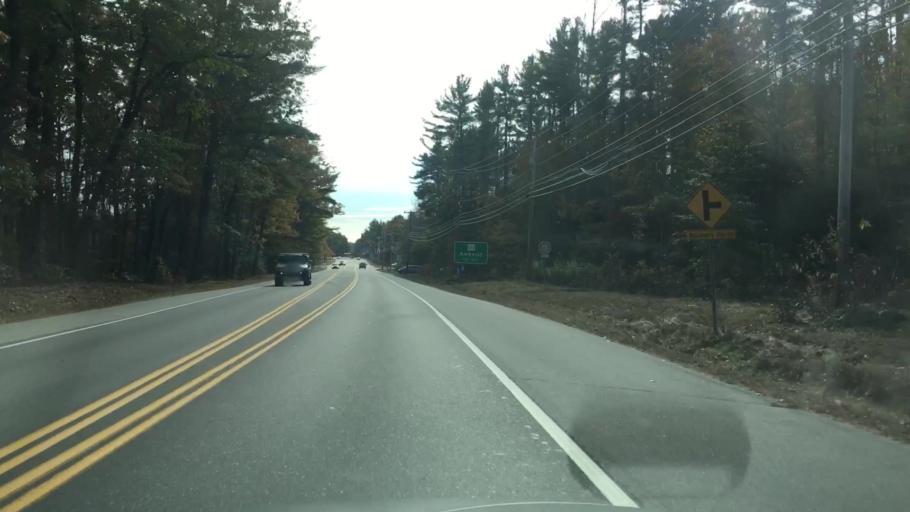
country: US
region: New Hampshire
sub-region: Hillsborough County
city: Milford
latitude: 42.8778
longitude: -71.6119
